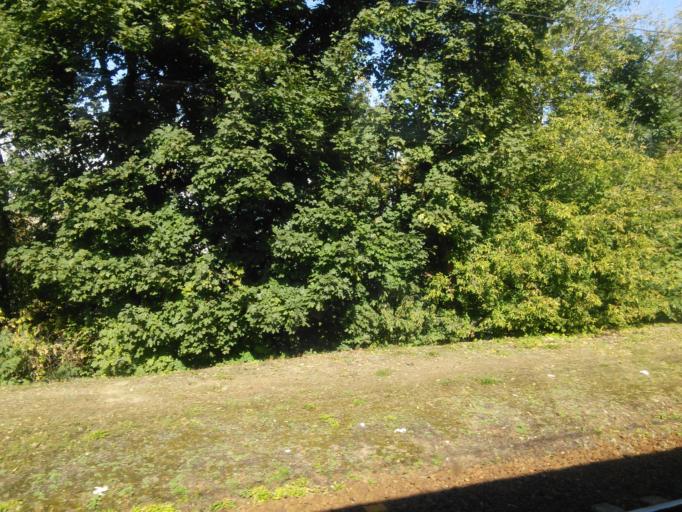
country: RU
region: Moscow
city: Taganskiy
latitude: 55.7499
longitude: 37.6740
